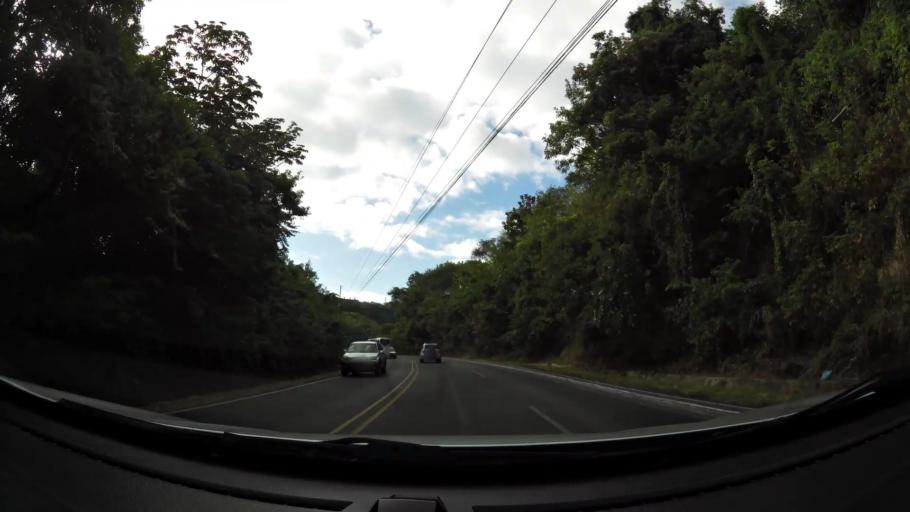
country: CR
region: Puntarenas
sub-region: Canton de Garabito
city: Jaco
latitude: 9.6812
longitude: -84.6483
